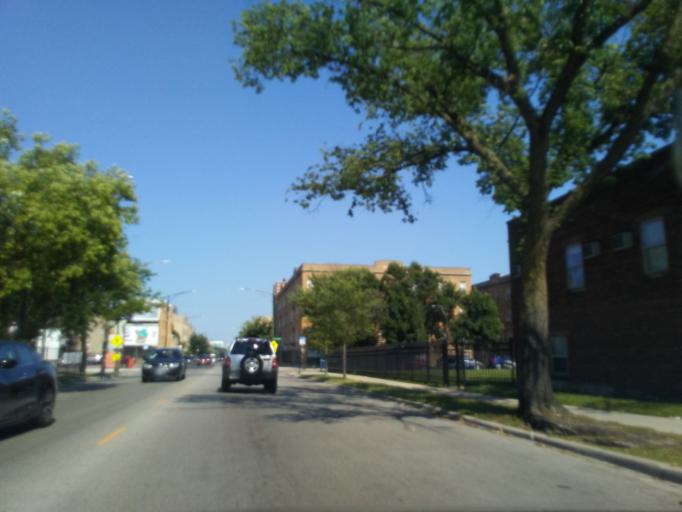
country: US
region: Illinois
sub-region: Cook County
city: Lincolnwood
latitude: 41.9757
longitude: -87.7167
